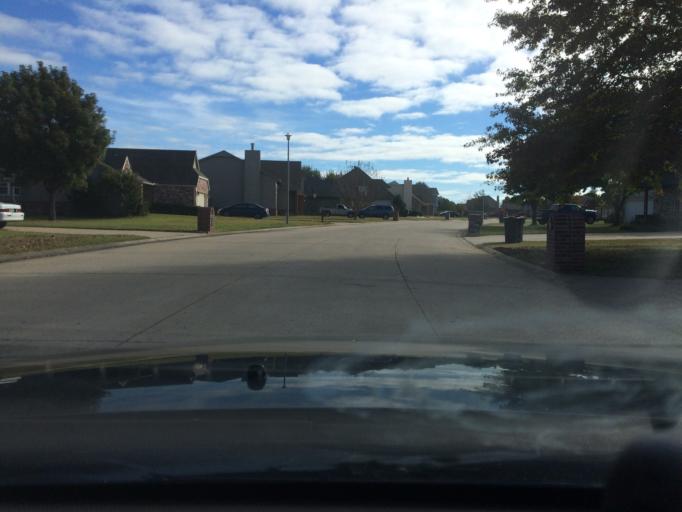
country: US
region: Oklahoma
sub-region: Tulsa County
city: Broken Arrow
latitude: 36.1107
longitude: -95.7593
